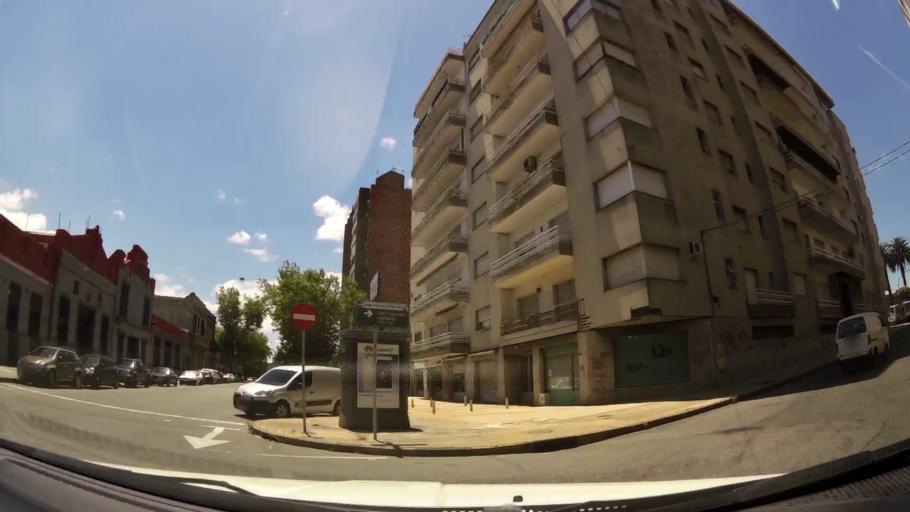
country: UY
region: Montevideo
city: Montevideo
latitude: -34.8860
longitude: -56.1935
